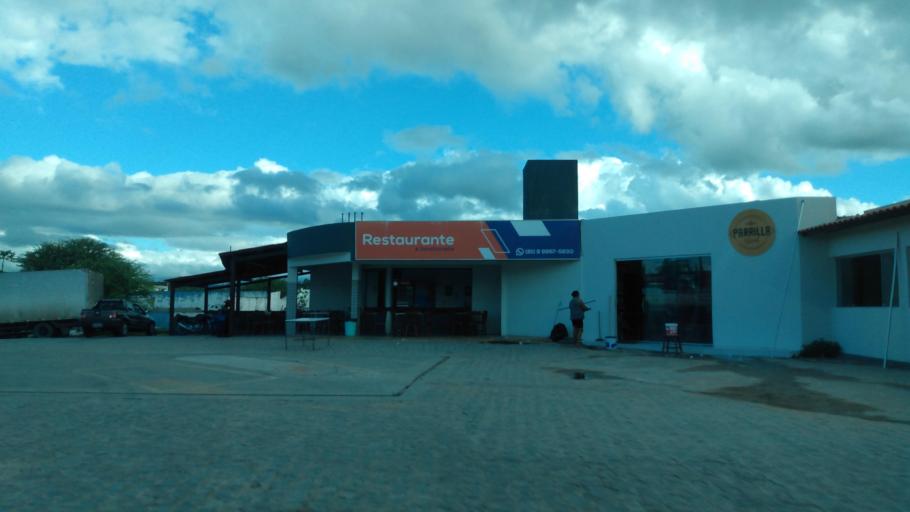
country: BR
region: Pernambuco
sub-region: Gravata
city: Gravata
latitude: -8.1963
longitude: -35.5704
